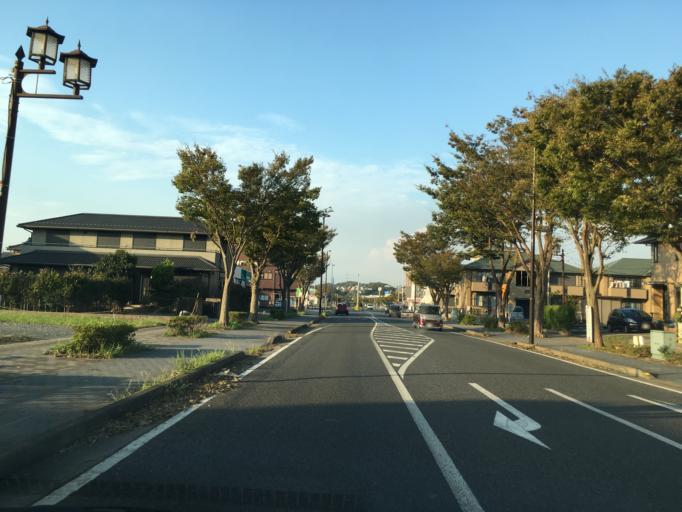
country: JP
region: Chiba
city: Kimitsu
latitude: 35.3295
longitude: 139.8923
